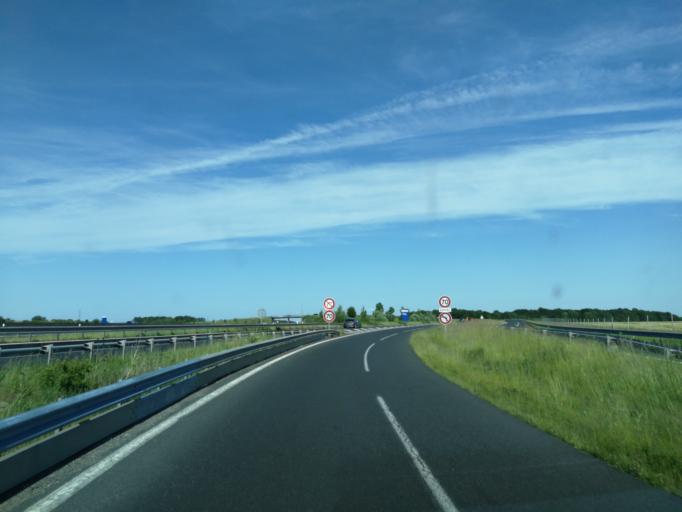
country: FR
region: Centre
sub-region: Departement d'Indre-et-Loire
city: Savonnieres
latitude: 47.3040
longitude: 0.5610
